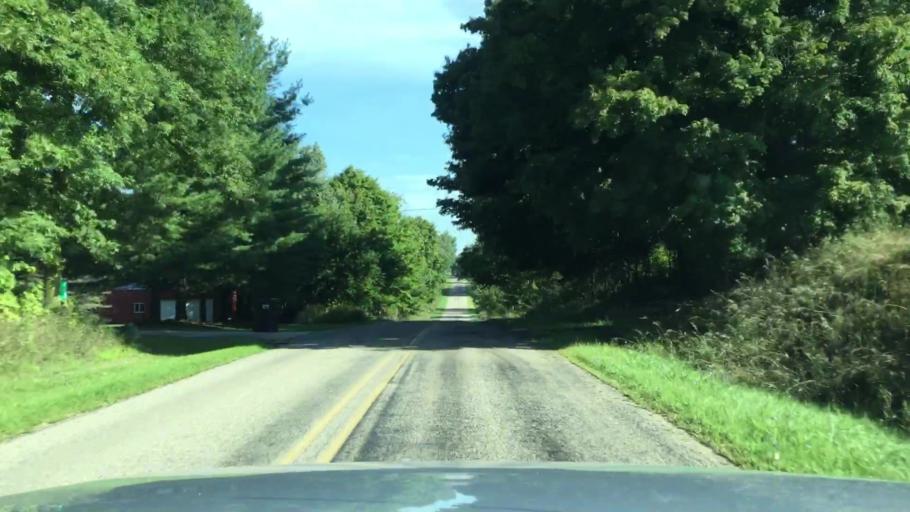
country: US
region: Michigan
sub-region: Lenawee County
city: Hudson
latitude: 41.8765
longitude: -84.4201
